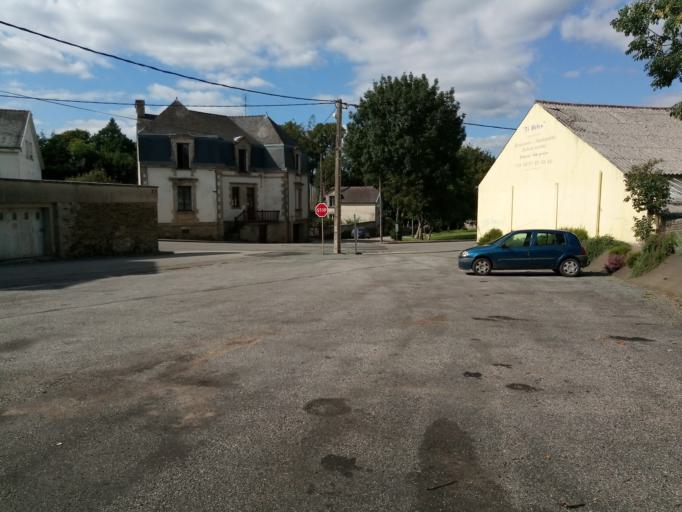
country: FR
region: Brittany
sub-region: Departement du Morbihan
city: Gourin
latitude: 48.1412
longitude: -3.6056
